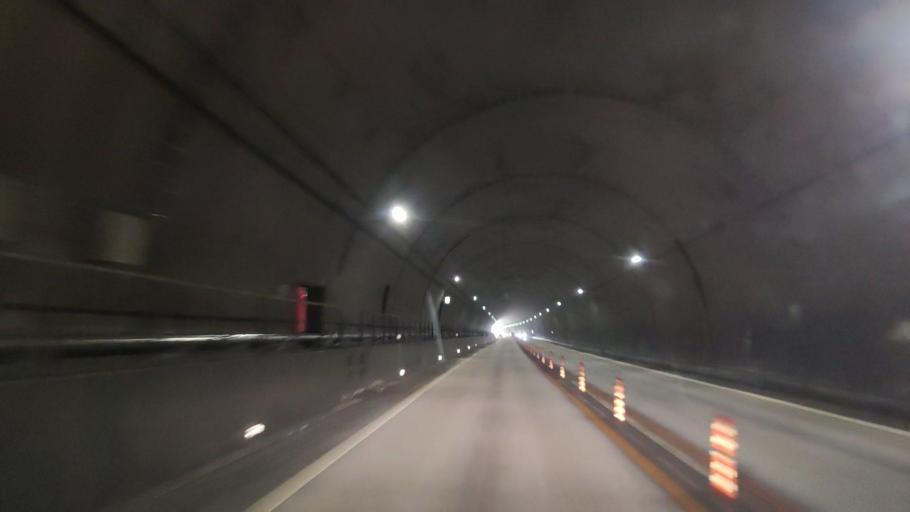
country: JP
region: Ehime
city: Hojo
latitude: 34.0843
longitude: 132.9776
